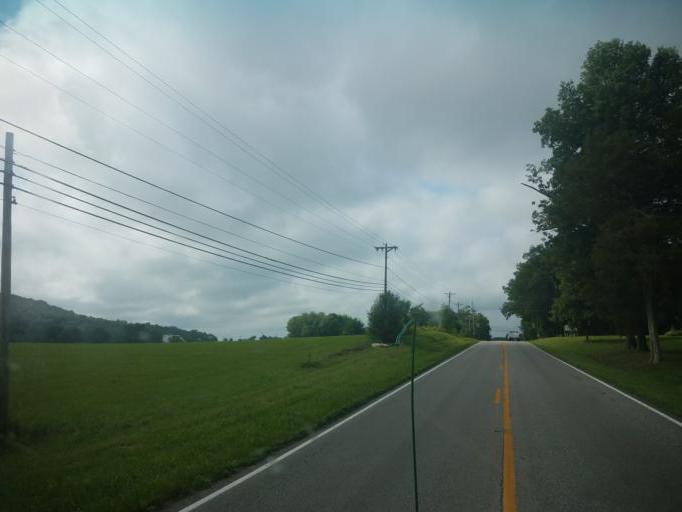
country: US
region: Kentucky
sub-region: Clinton County
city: Albany
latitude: 36.7153
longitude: -85.1349
